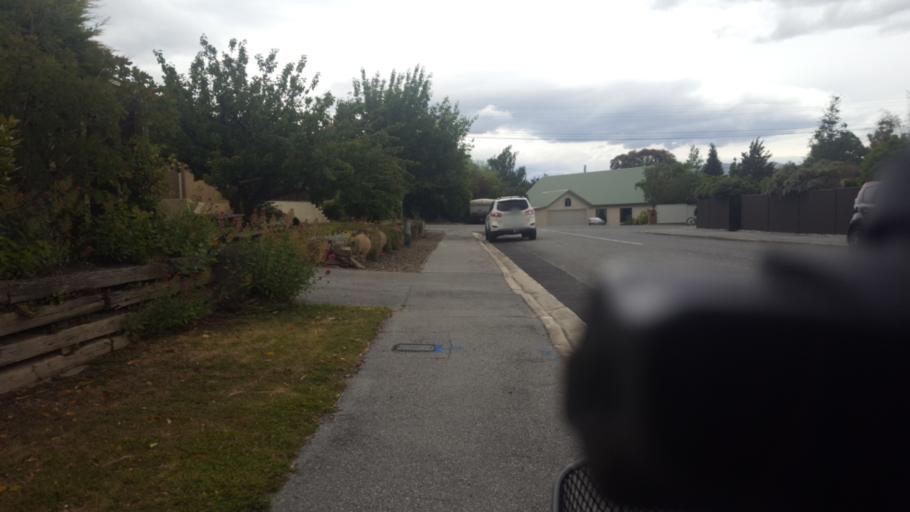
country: NZ
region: Otago
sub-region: Queenstown-Lakes District
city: Wanaka
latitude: -45.2620
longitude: 169.3794
